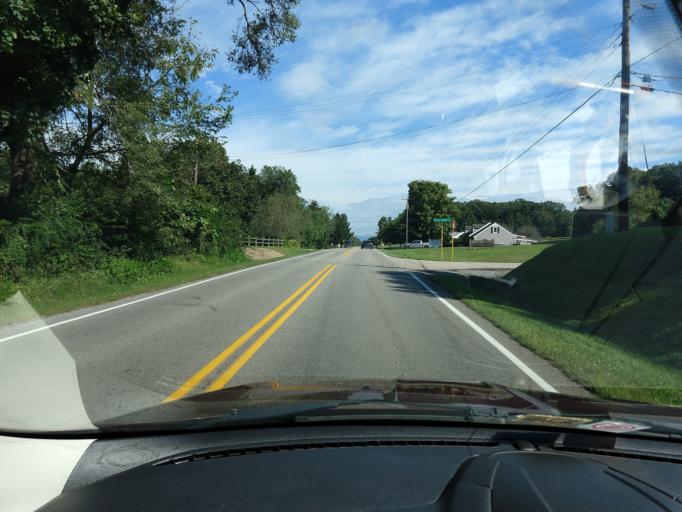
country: US
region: Virginia
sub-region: Rockingham County
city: Grottoes
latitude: 38.2433
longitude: -78.8281
